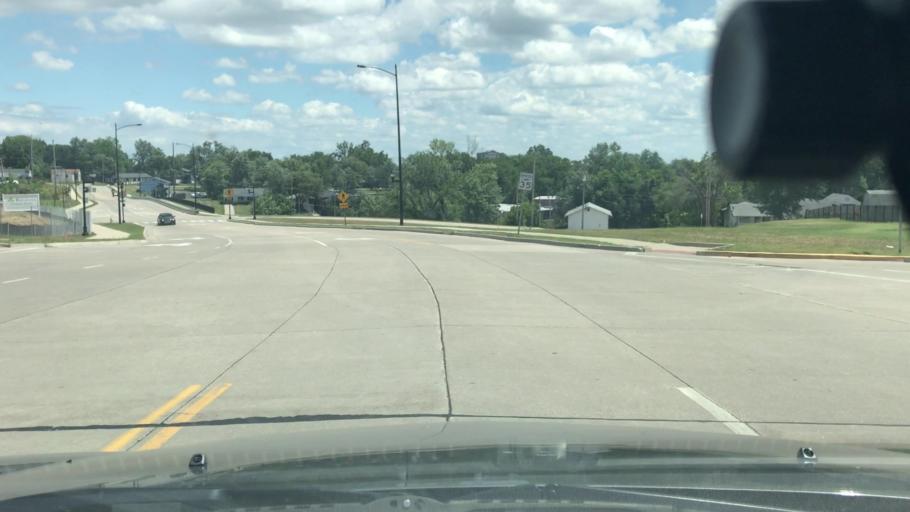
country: US
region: Missouri
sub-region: Saint Charles County
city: Saint Charles
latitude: 38.7819
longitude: -90.5043
